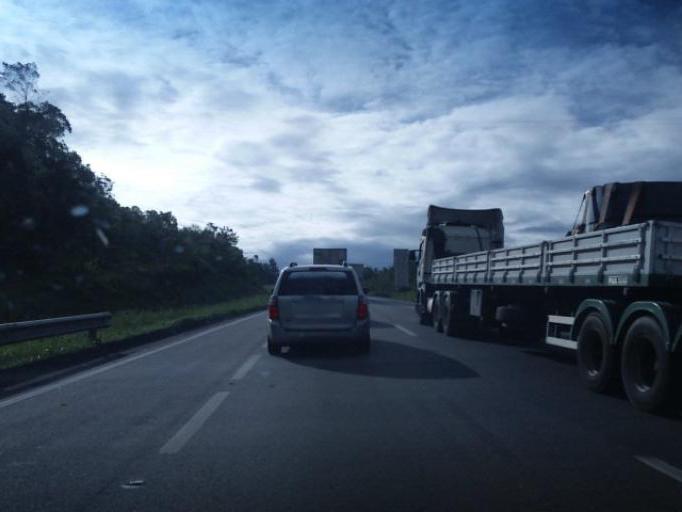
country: BR
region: Parana
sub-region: Antonina
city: Antonina
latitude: -25.1101
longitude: -48.7577
